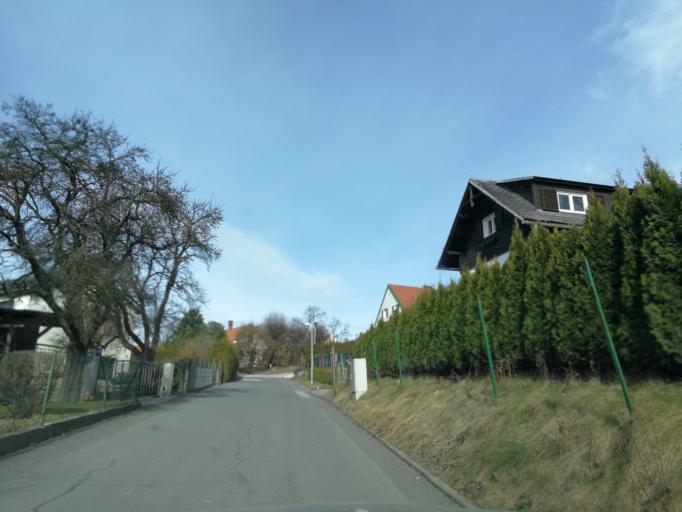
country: AT
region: Styria
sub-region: Politischer Bezirk Weiz
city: Gleisdorf
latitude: 47.1178
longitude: 15.7106
